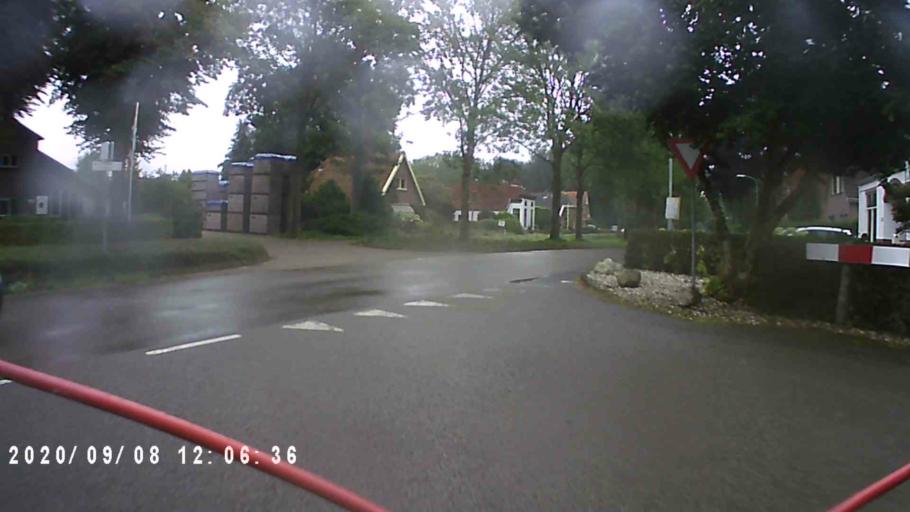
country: NL
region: Groningen
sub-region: Gemeente Veendam
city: Veendam
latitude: 53.1080
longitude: 6.8257
